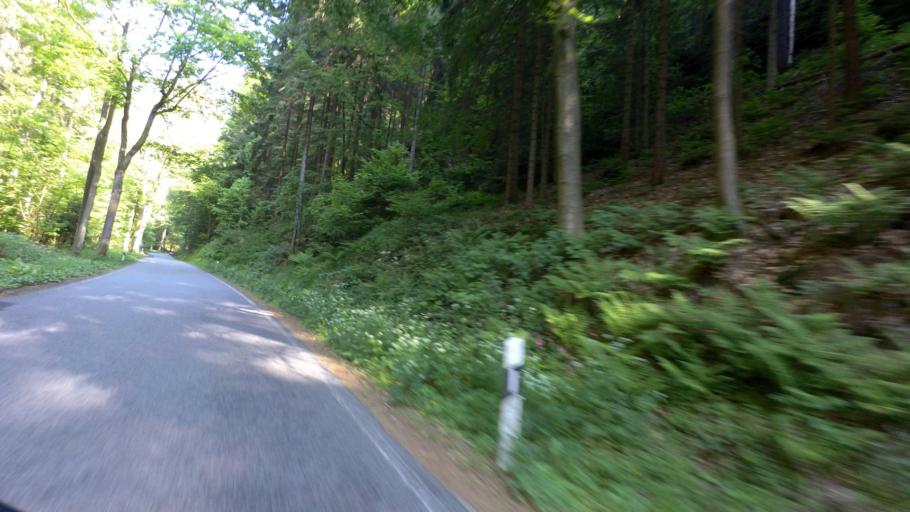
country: DE
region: Saxony
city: Porschdorf
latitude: 50.9518
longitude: 14.1335
